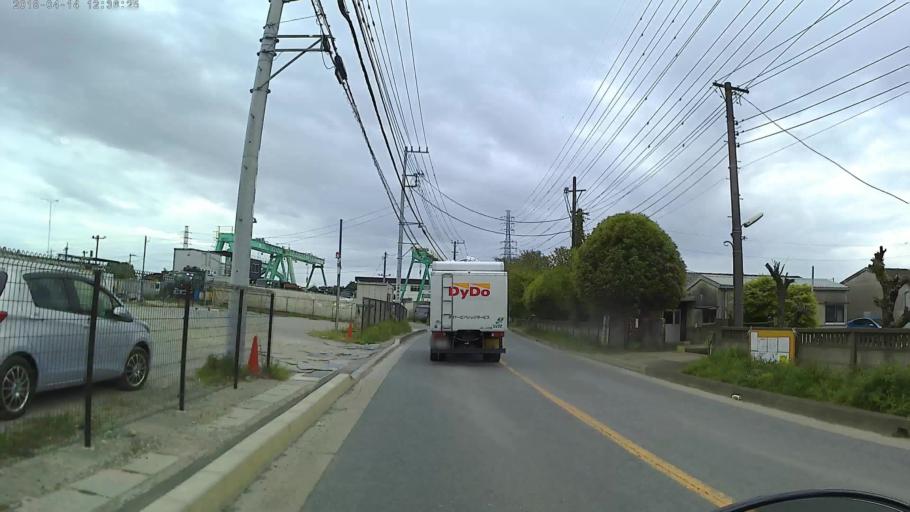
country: JP
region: Kanagawa
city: Atsugi
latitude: 35.4162
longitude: 139.4077
